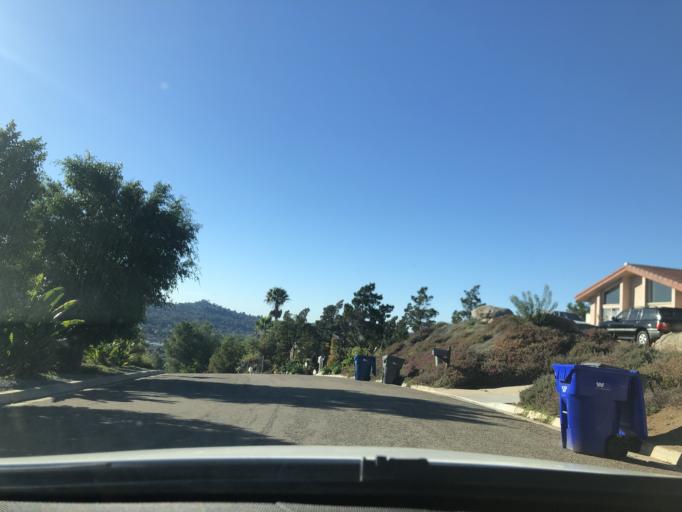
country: US
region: California
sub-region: San Diego County
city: Bostonia
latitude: 32.7821
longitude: -116.9397
